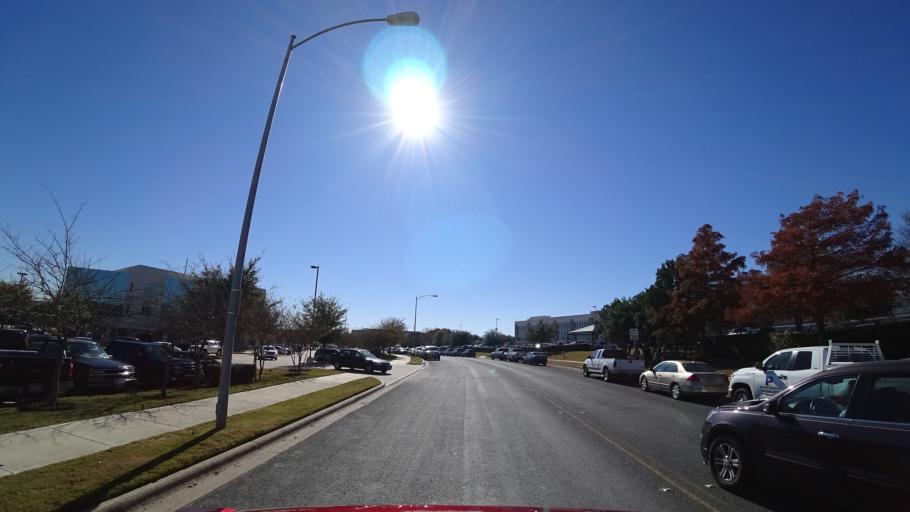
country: US
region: Texas
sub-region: Travis County
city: Wells Branch
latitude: 30.4126
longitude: -97.7040
